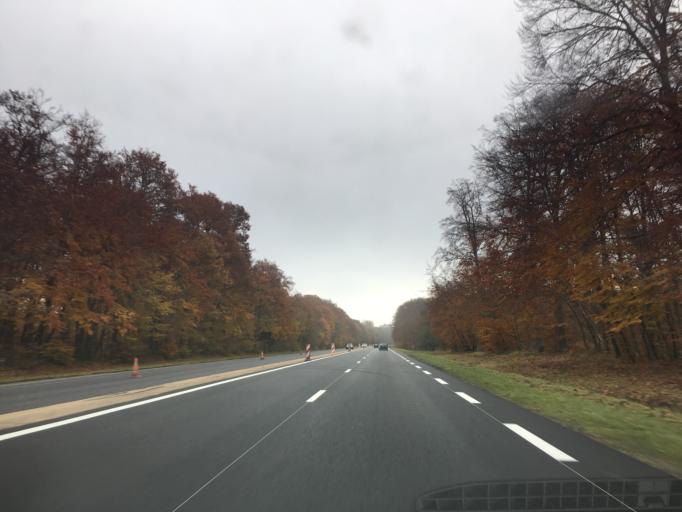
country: FR
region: Ile-de-France
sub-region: Departement de Seine-et-Marne
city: Avon
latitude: 48.3960
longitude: 2.7302
